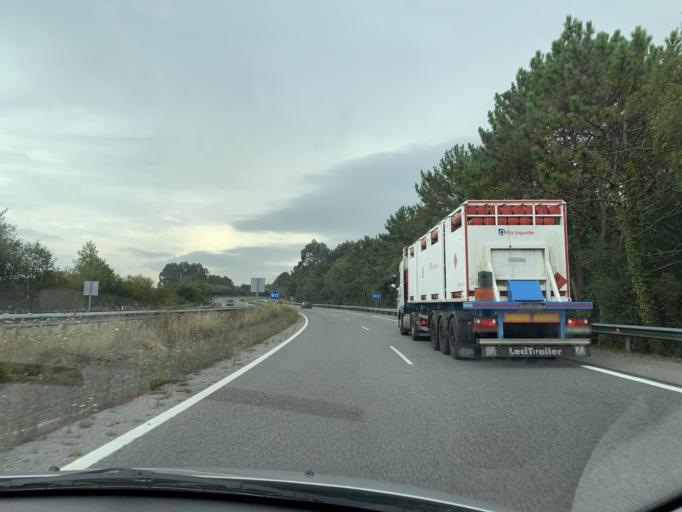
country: ES
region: Asturias
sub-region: Province of Asturias
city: Salas
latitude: 43.5501
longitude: -6.3137
